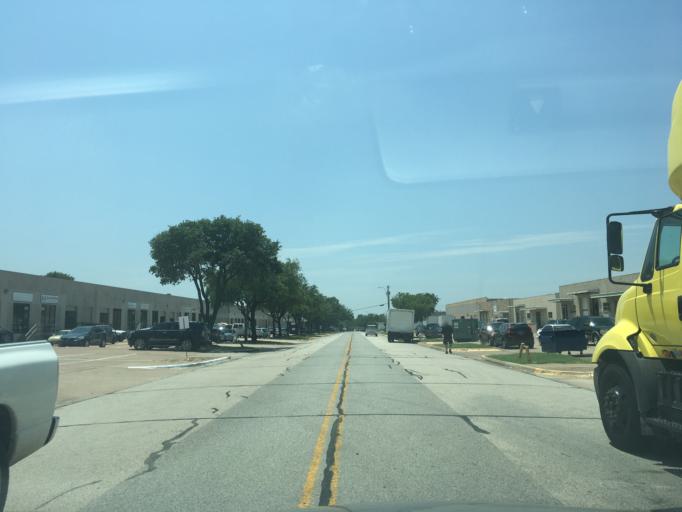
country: US
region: Texas
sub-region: Dallas County
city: Carrollton
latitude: 32.9503
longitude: -96.8653
